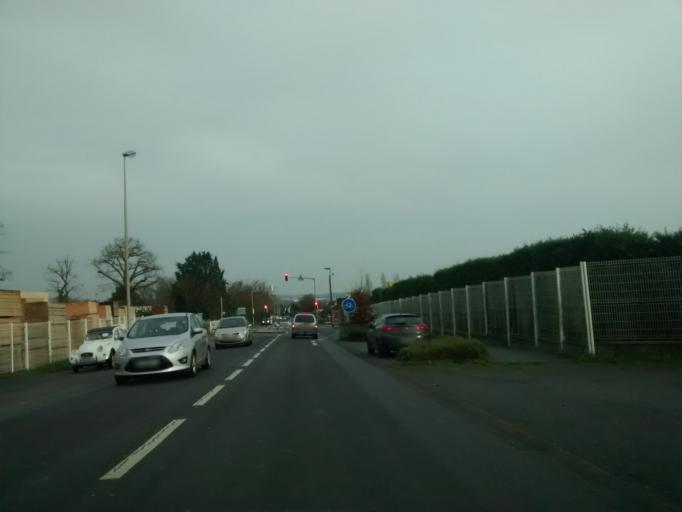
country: FR
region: Brittany
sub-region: Departement d'Ille-et-Vilaine
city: Noyal-sur-Vilaine
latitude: 48.1115
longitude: -1.5327
